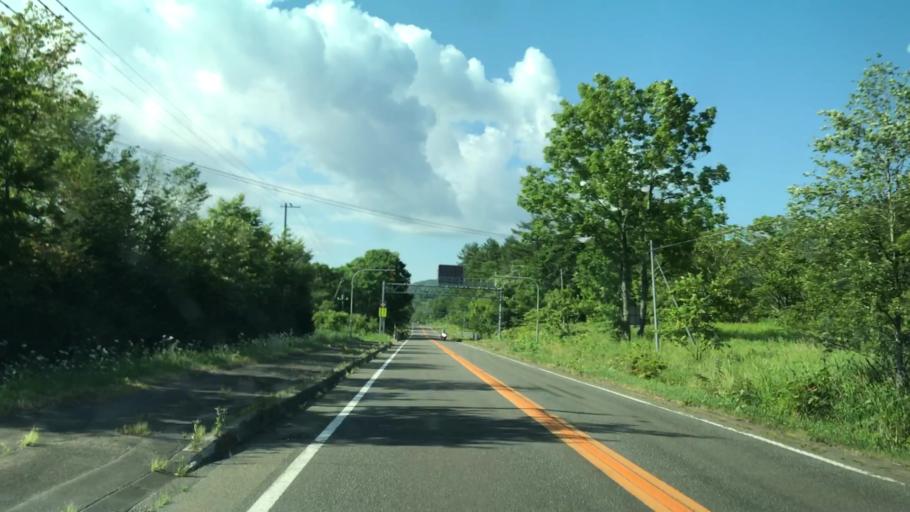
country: JP
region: Hokkaido
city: Shimo-furano
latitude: 42.8885
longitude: 142.4316
